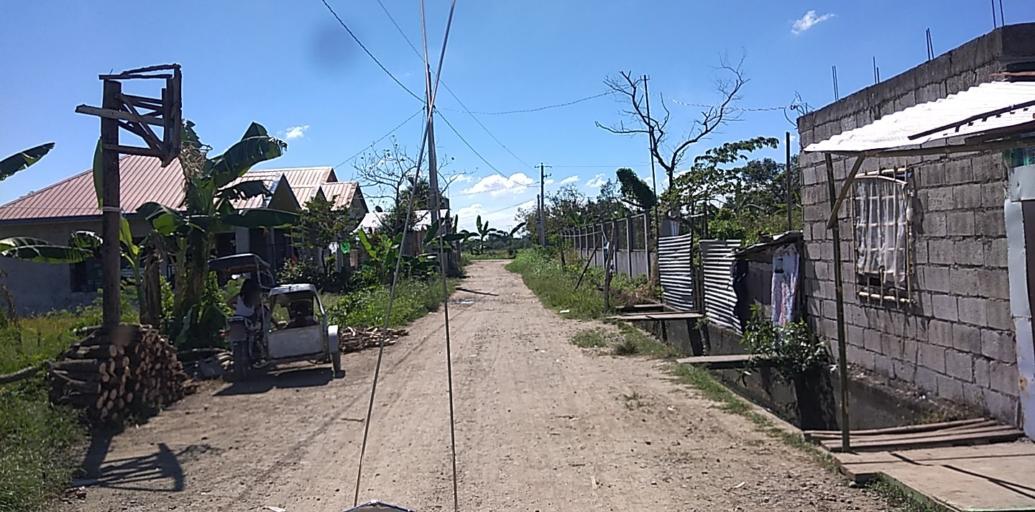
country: PH
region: Central Luzon
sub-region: Province of Pampanga
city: Arayat
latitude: 15.1282
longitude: 120.7858
